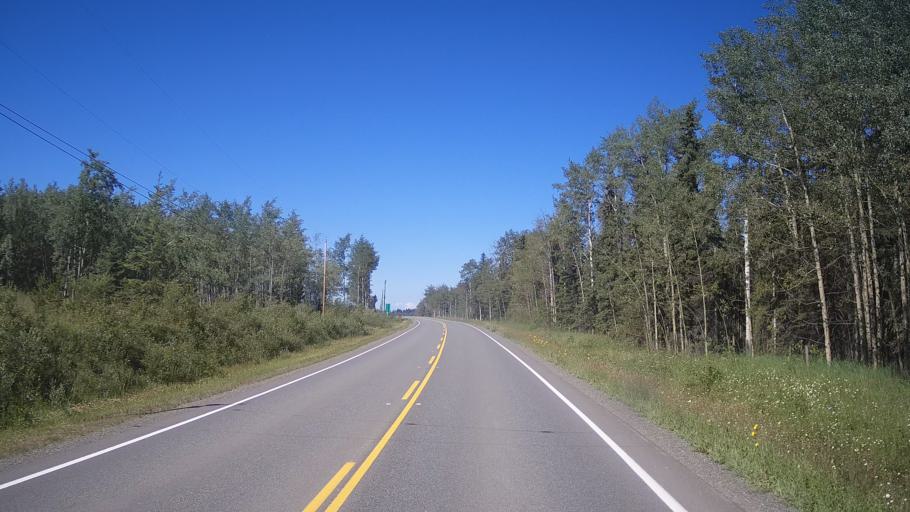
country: CA
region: British Columbia
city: Cache Creek
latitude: 51.5451
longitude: -120.9423
